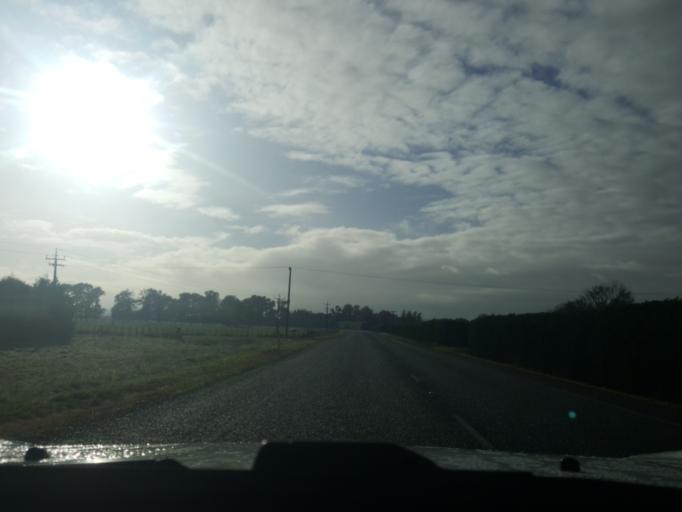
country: NZ
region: Waikato
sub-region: Waipa District
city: Cambridge
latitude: -37.7801
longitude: 175.3964
